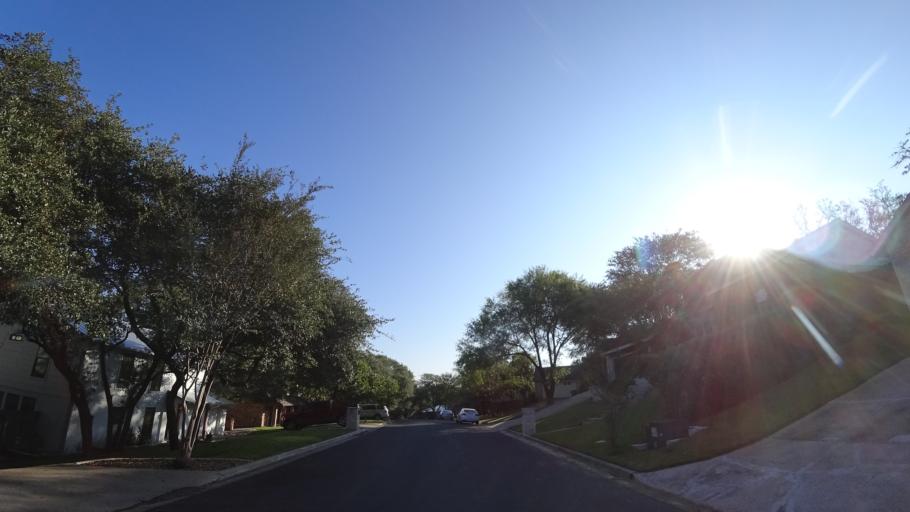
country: US
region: Texas
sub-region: Travis County
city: Rollingwood
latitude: 30.2634
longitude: -97.8068
